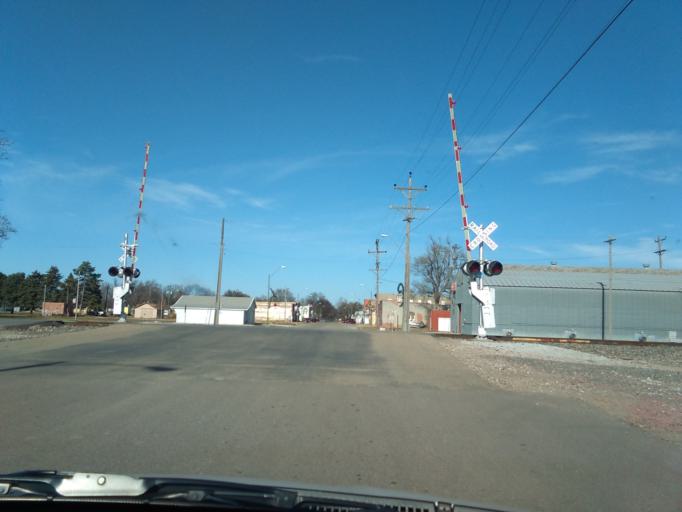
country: US
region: Nebraska
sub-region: Clay County
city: Harvard
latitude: 40.6164
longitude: -98.0972
